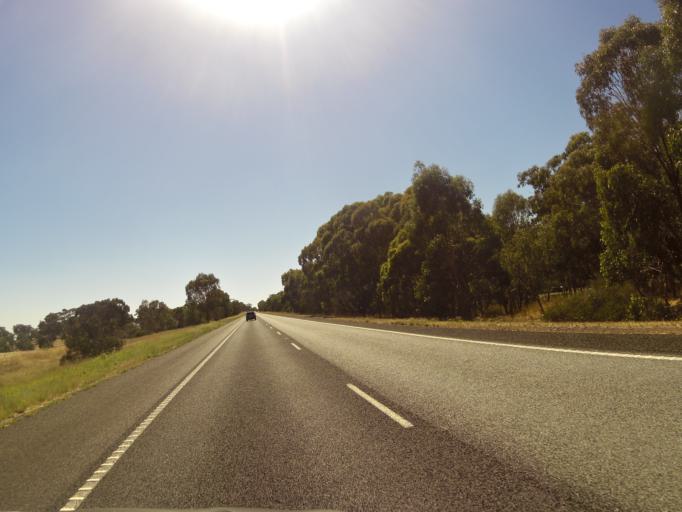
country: AU
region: Victoria
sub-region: Greater Shepparton
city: Shepparton
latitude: -36.8385
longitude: 145.3686
